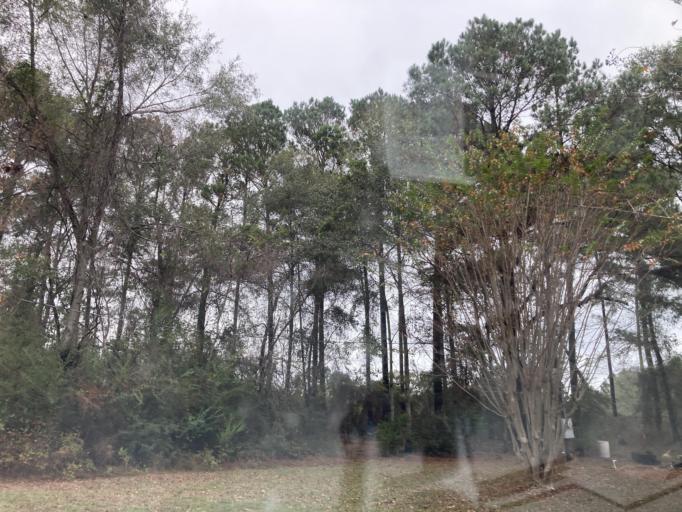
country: US
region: Mississippi
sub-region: Lamar County
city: Purvis
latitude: 31.1855
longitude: -89.4242
